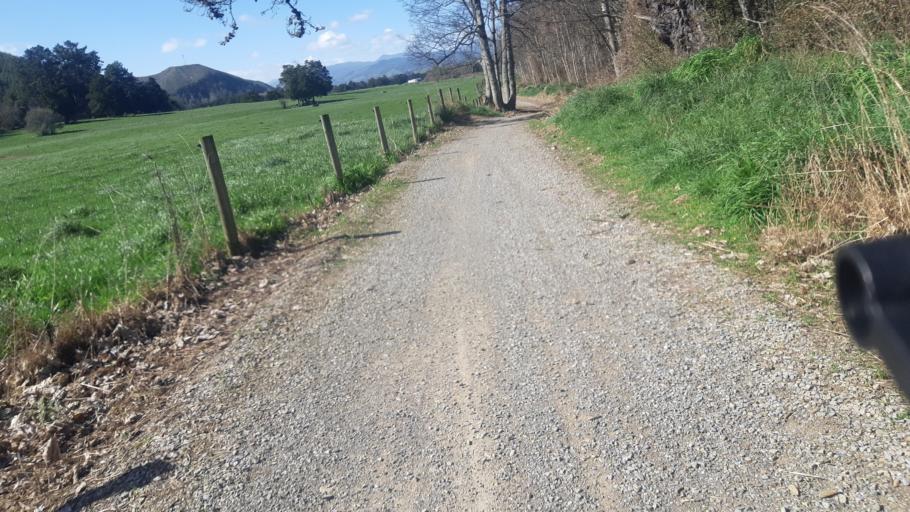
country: NZ
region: Tasman
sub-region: Tasman District
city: Wakefield
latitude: -41.4054
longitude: 173.0172
